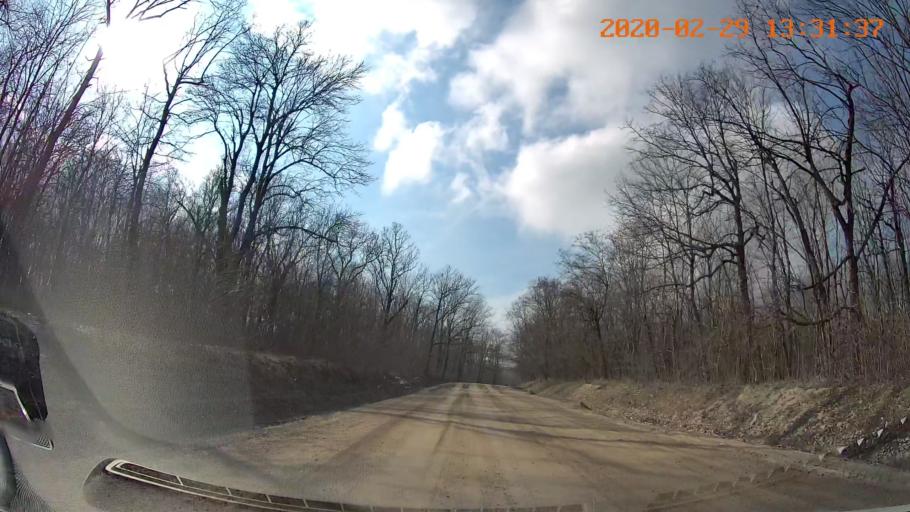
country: MD
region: Telenesti
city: Camenca
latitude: 47.8816
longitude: 28.6175
